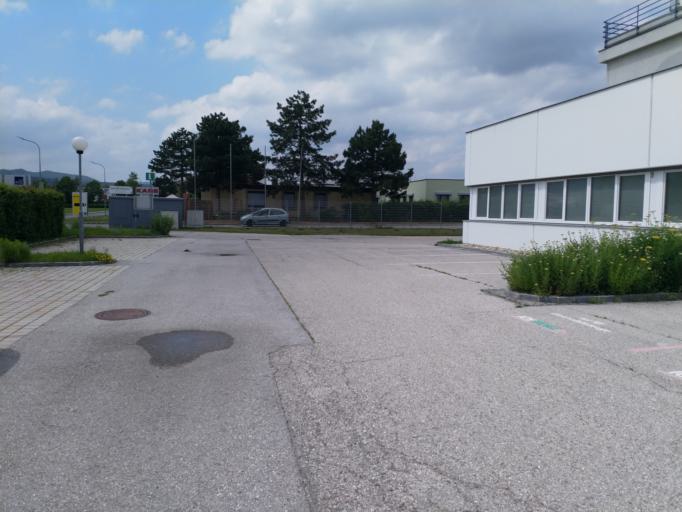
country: AT
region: Lower Austria
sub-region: Politischer Bezirk Modling
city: Wiener Neudorf
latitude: 48.0751
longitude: 16.3217
